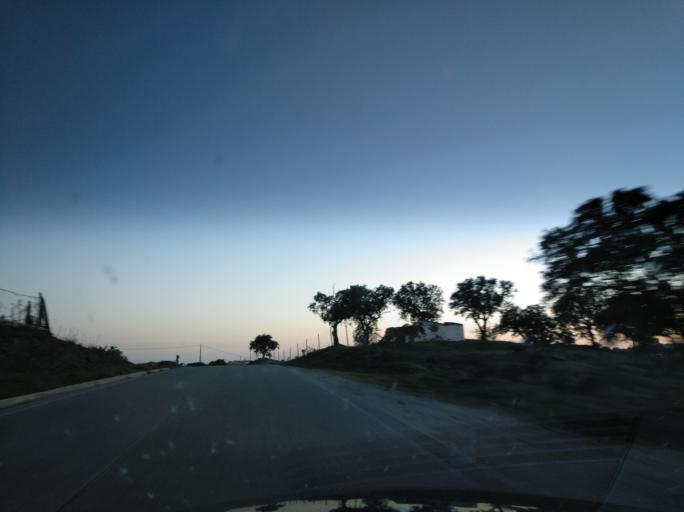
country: PT
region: Faro
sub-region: Vila Real de Santo Antonio
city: Monte Gordo
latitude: 37.2108
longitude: -7.5198
